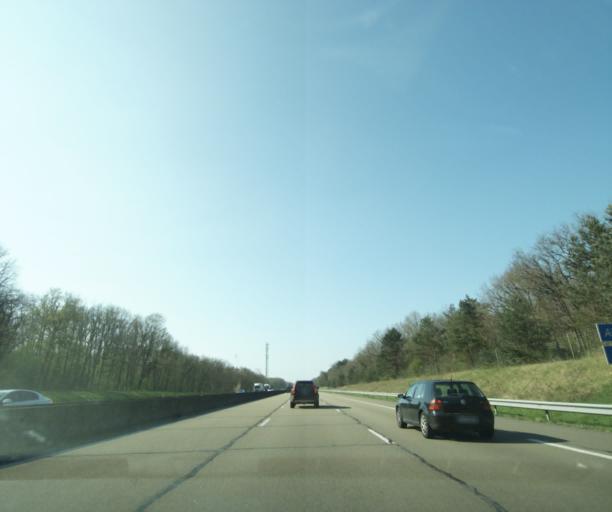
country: FR
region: Ile-de-France
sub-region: Departement de Seine-et-Marne
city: Bagneaux-sur-Loing
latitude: 48.2455
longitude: 2.7435
